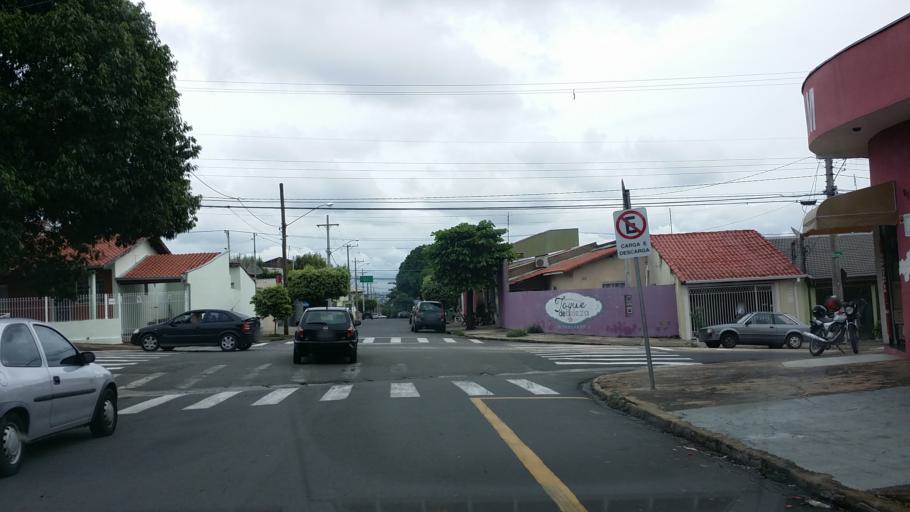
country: BR
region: Sao Paulo
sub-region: Indaiatuba
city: Indaiatuba
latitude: -23.1218
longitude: -47.2280
